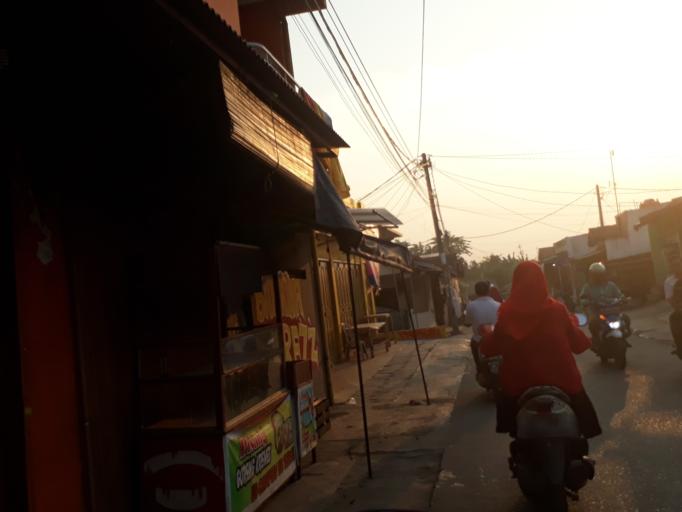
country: ID
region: West Java
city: Bekasi
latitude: -6.2439
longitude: 107.0561
